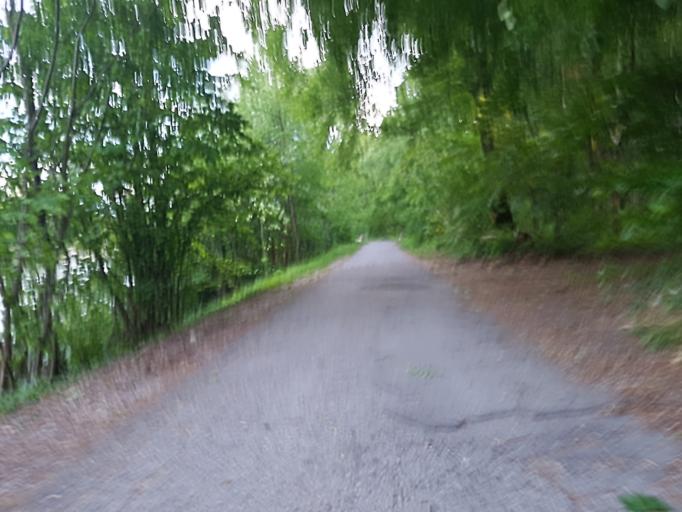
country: AT
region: Salzburg
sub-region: Politischer Bezirk Salzburg-Umgebung
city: Anif
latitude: 47.7692
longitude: 13.0741
